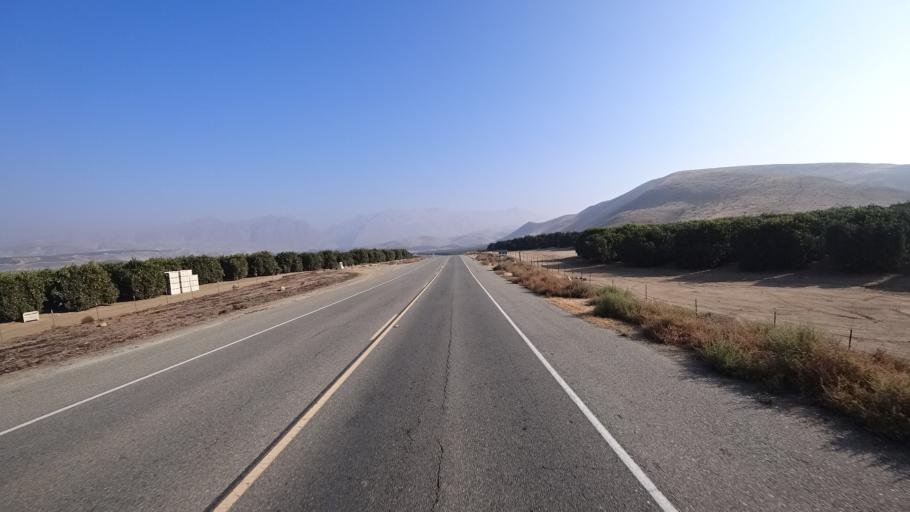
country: US
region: California
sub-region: Kern County
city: Lamont
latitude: 35.4158
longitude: -118.8338
